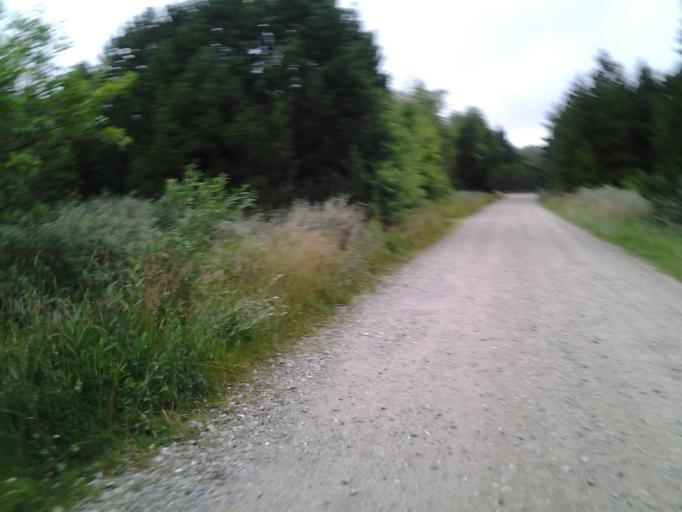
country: DE
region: Schleswig-Holstein
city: List
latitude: 55.1547
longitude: 8.5230
